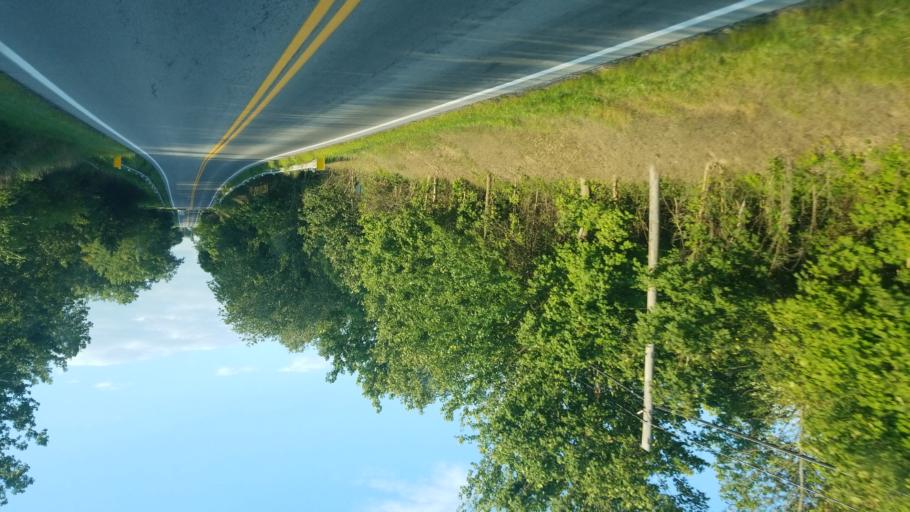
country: US
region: Ohio
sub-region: Huron County
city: Willard
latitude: 41.0788
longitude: -82.7178
